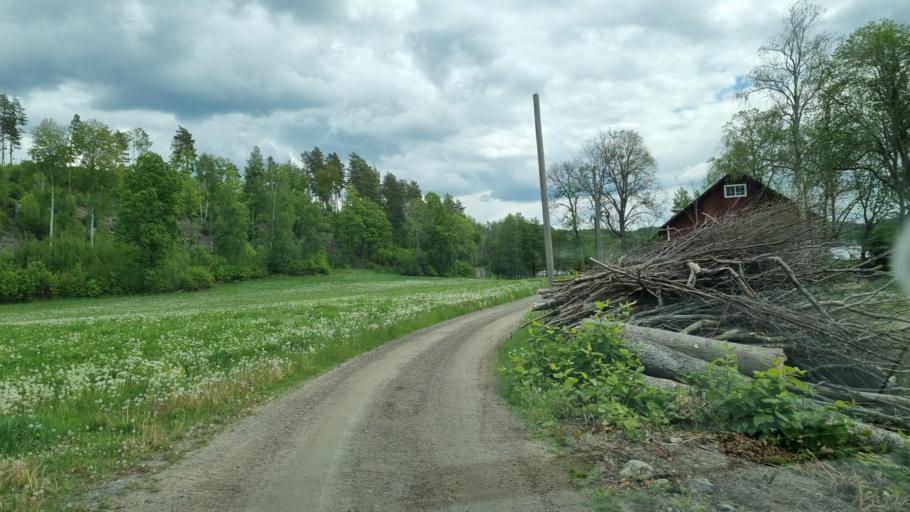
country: SE
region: OEstergoetland
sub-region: Atvidabergs Kommun
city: Atvidaberg
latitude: 58.1906
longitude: 16.0442
